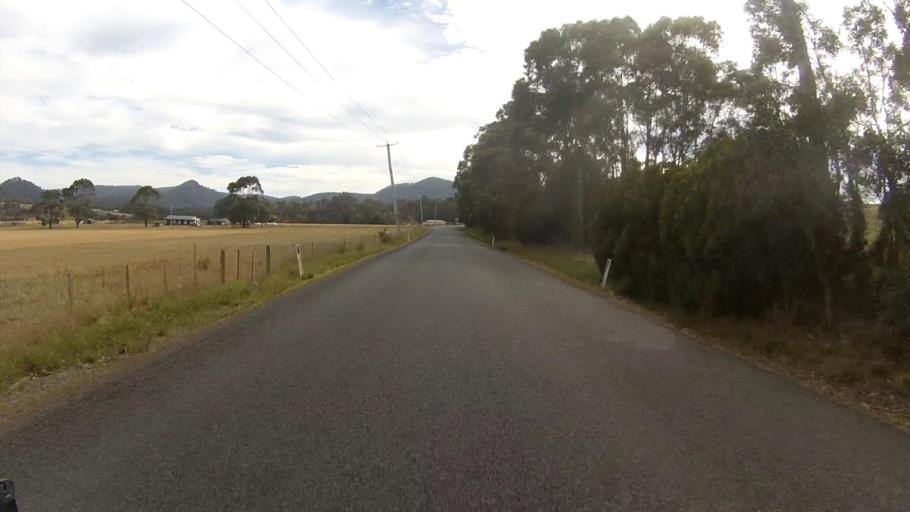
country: AU
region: Tasmania
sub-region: Sorell
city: Sorell
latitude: -42.7920
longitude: 147.7989
